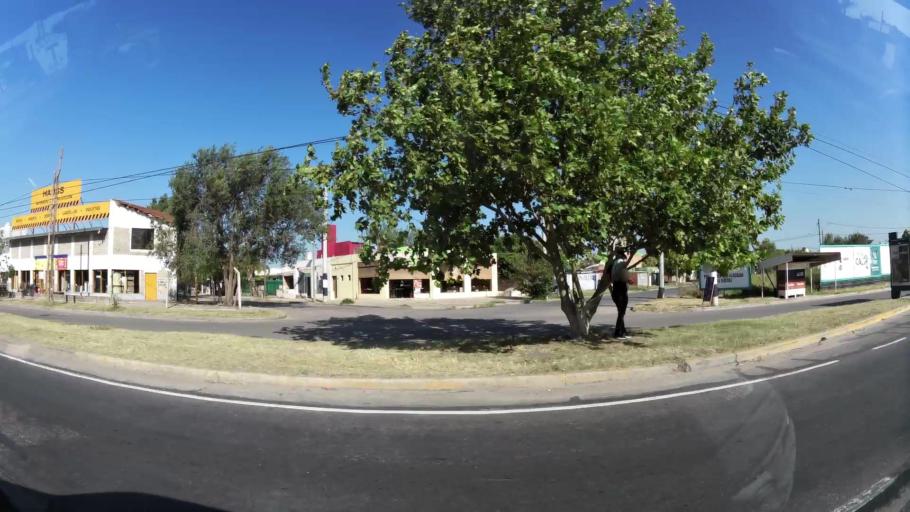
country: AR
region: Cordoba
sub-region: Departamento de Capital
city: Cordoba
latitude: -31.4734
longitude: -64.2318
